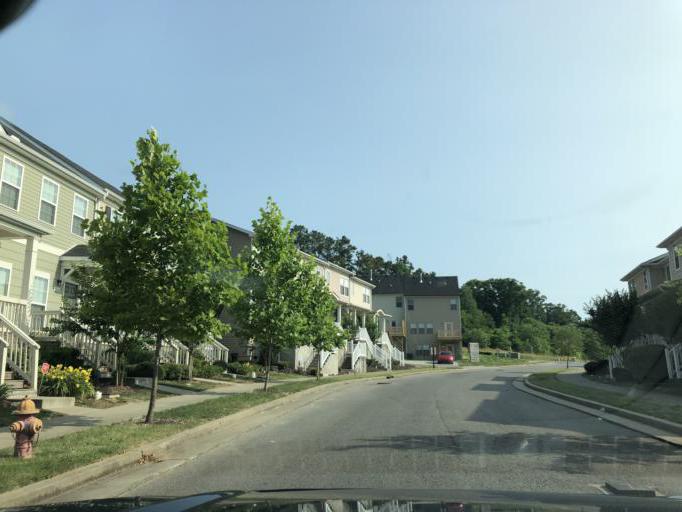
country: US
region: Tennessee
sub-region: Rutherford County
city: La Vergne
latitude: 36.0509
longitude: -86.6431
